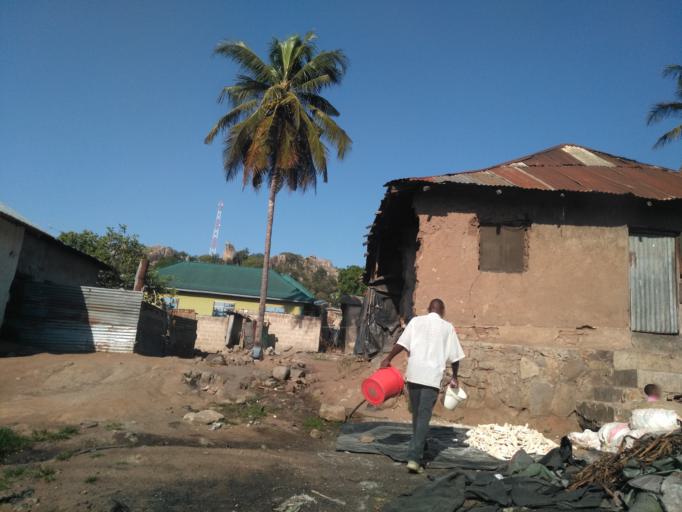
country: TZ
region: Mwanza
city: Mwanza
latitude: -2.5030
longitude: 32.8914
